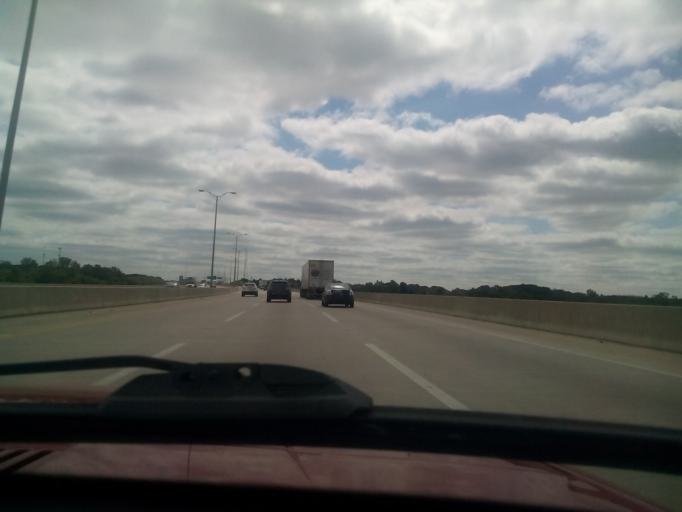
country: US
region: Illinois
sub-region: Cook County
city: Lemont
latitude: 41.6681
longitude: -88.0277
